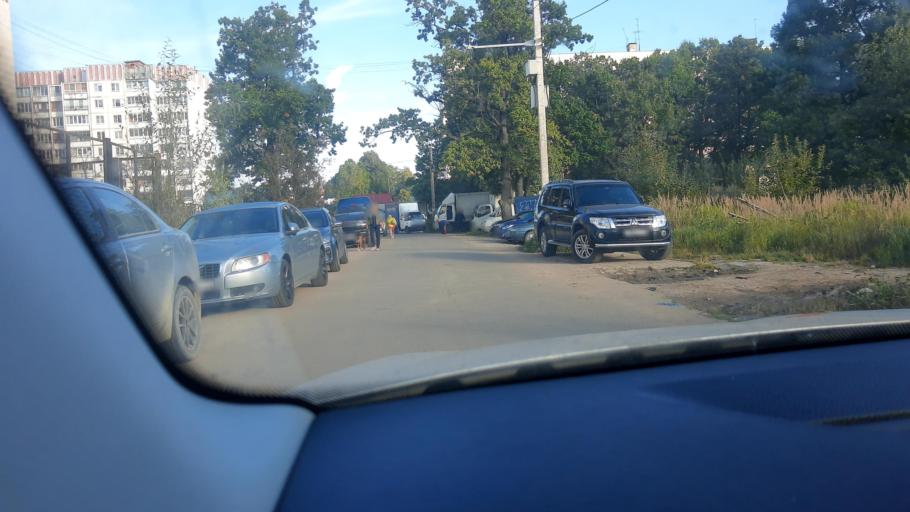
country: RU
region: Moskovskaya
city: Selyatino
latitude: 55.5509
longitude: 36.9730
